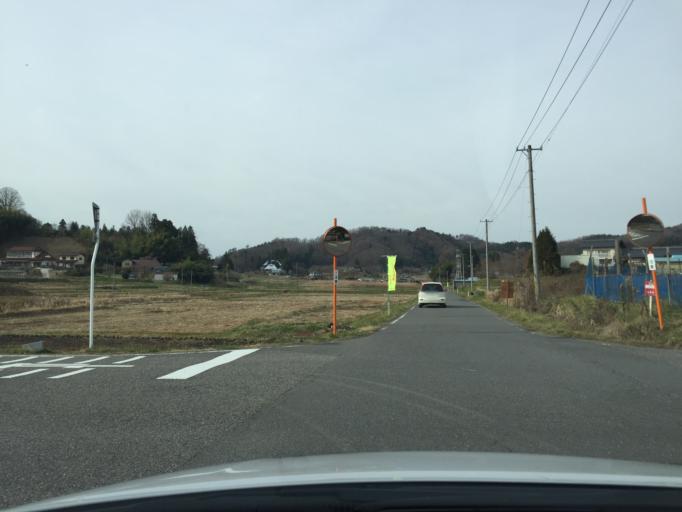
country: JP
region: Fukushima
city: Funehikimachi-funehiki
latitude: 37.4140
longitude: 140.5790
